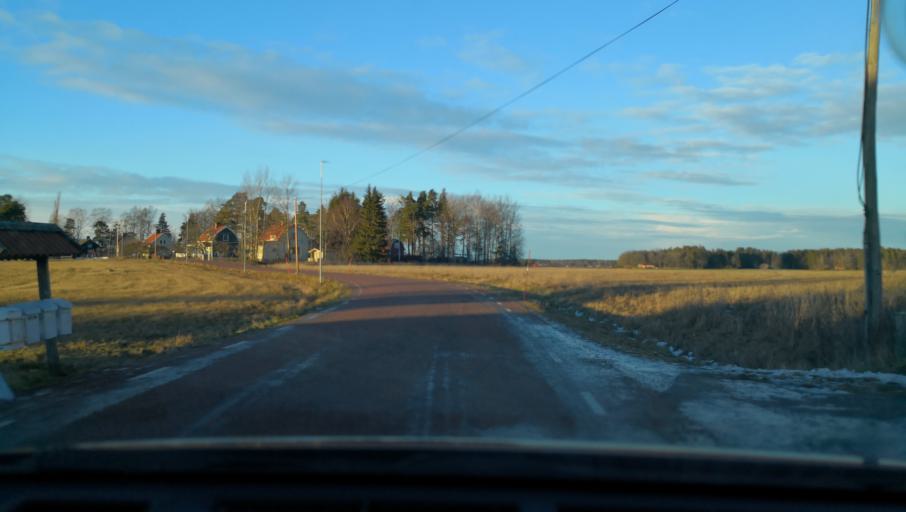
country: SE
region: Vaestmanland
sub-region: Vasteras
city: Tillberga
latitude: 59.6911
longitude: 16.6076
